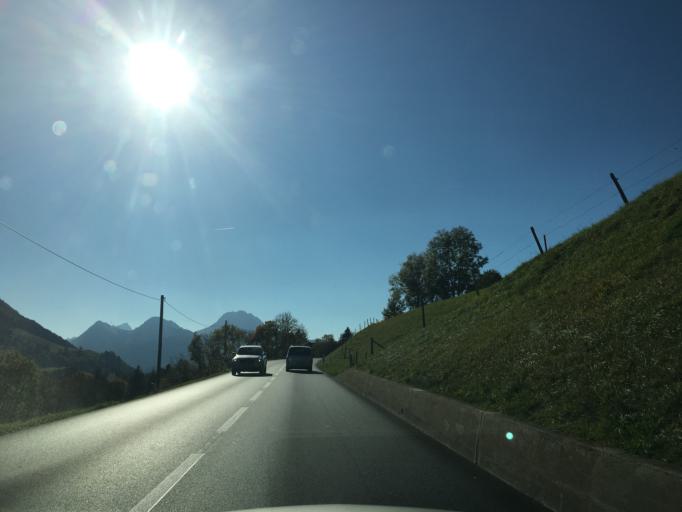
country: CH
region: Fribourg
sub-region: Gruyere District
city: Charmey
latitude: 46.6160
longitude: 7.1345
